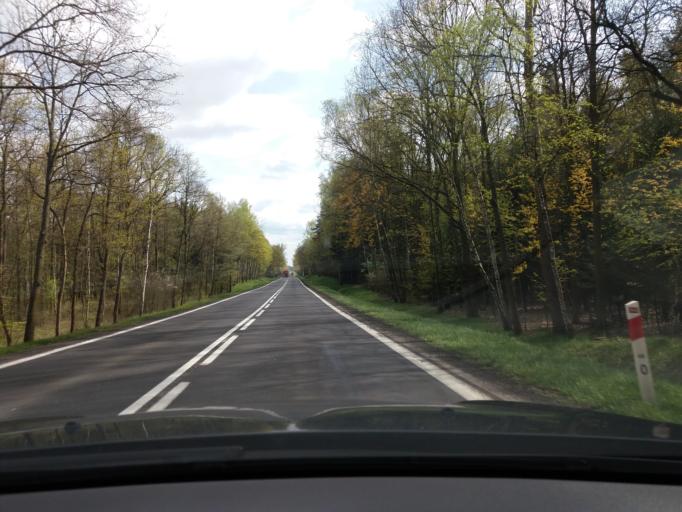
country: PL
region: Lower Silesian Voivodeship
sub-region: Powiat legnicki
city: Prochowice
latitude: 51.2486
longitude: 16.4055
